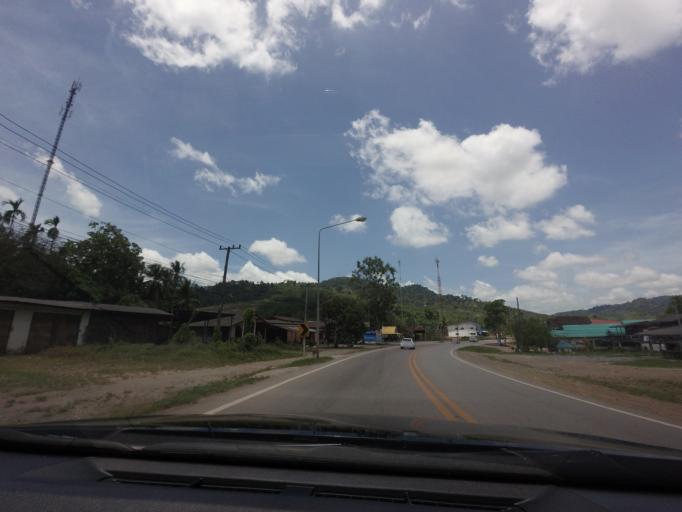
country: TH
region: Chumphon
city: Ban Nam Yuen
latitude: 9.9116
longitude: 98.9152
